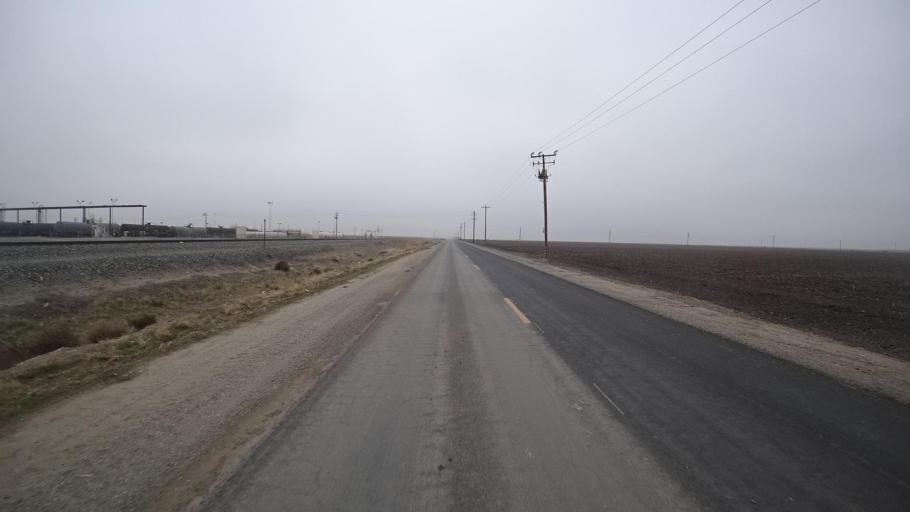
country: US
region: California
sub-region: Kern County
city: Greenfield
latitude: 35.1800
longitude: -119.1600
